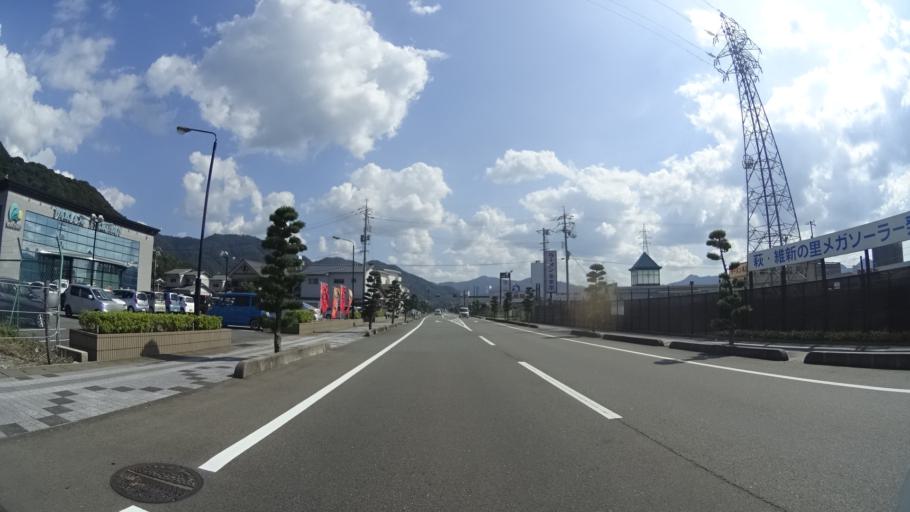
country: JP
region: Yamaguchi
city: Hagi
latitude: 34.4196
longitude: 131.4130
